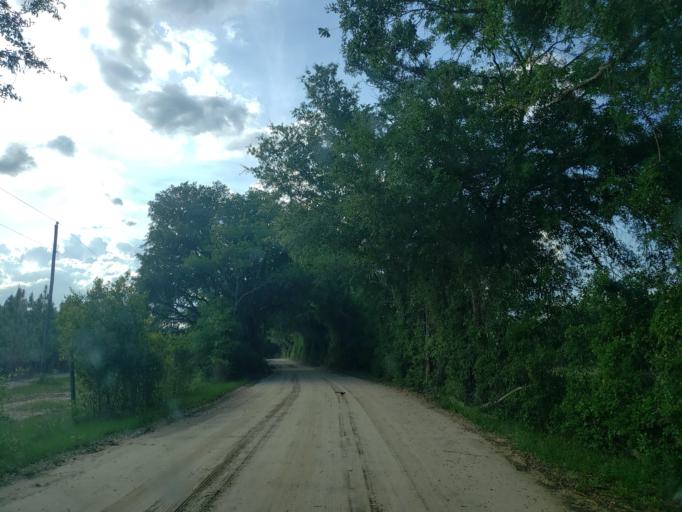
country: US
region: Georgia
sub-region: Echols County
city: Statenville
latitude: 30.6302
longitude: -83.1914
